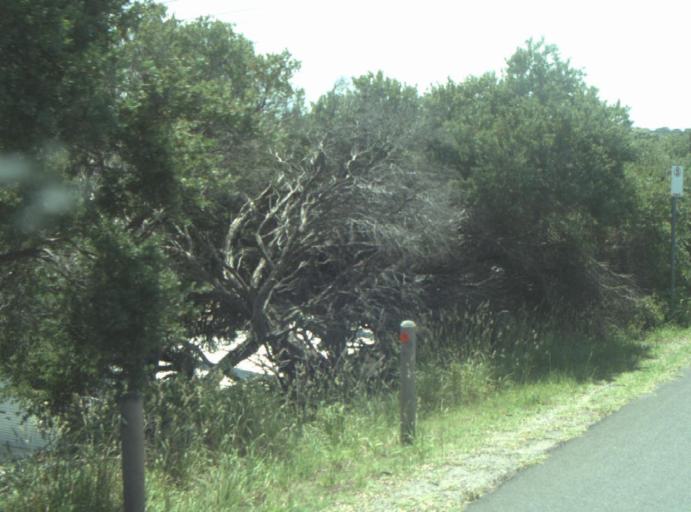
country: AU
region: Victoria
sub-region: Greater Geelong
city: Leopold
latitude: -38.2721
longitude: 144.5110
